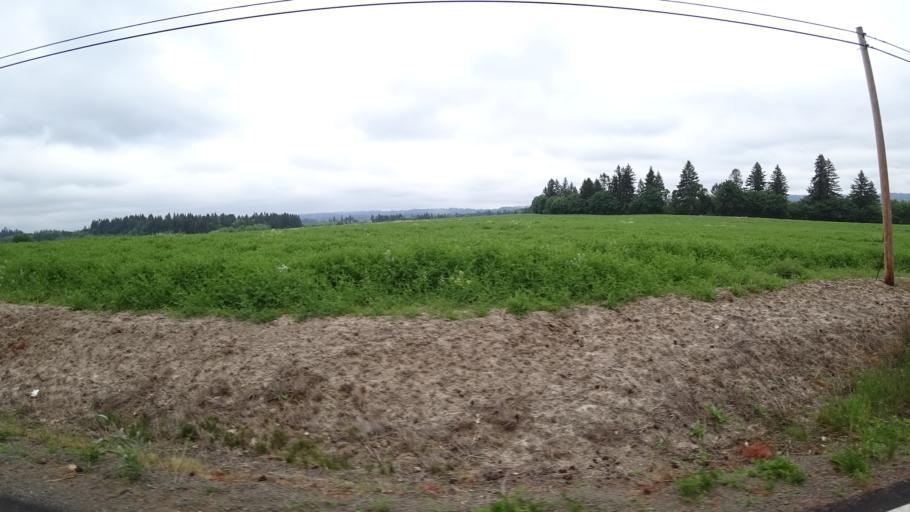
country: US
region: Oregon
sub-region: Washington County
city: Rockcreek
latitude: 45.5600
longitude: -122.8812
